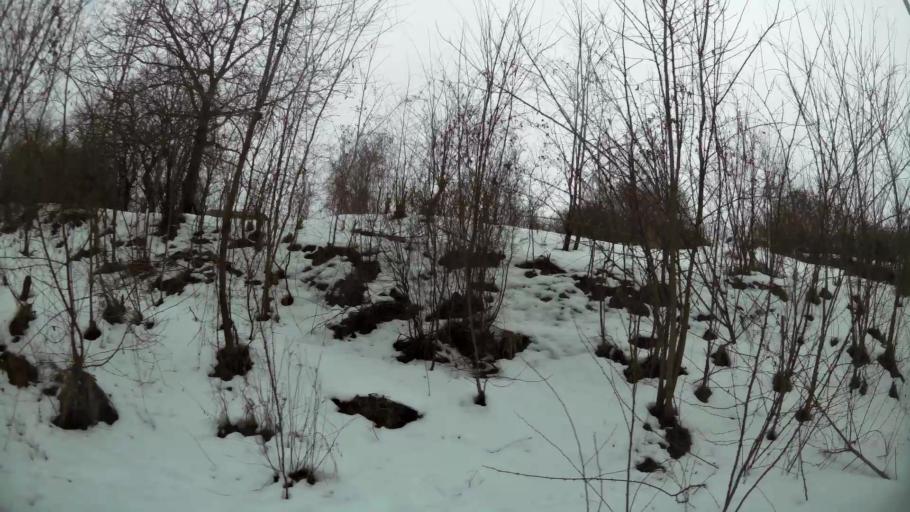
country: RS
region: Central Serbia
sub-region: Belgrade
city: Zvezdara
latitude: 44.7486
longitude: 20.5170
